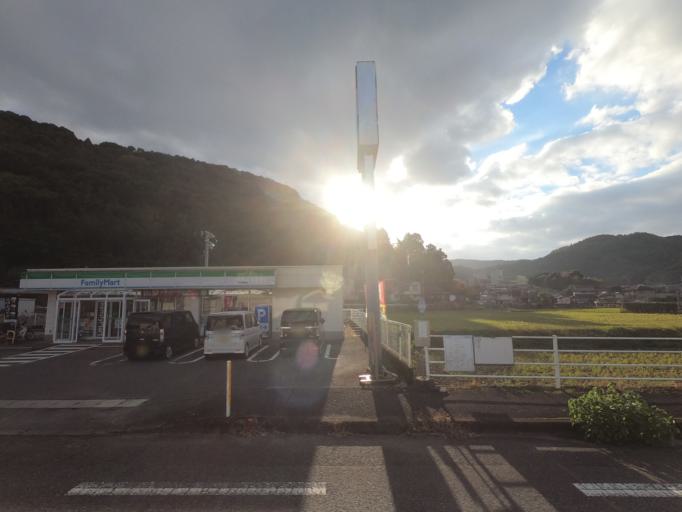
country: JP
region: Kumamoto
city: Minamata
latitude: 32.2684
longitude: 130.5048
